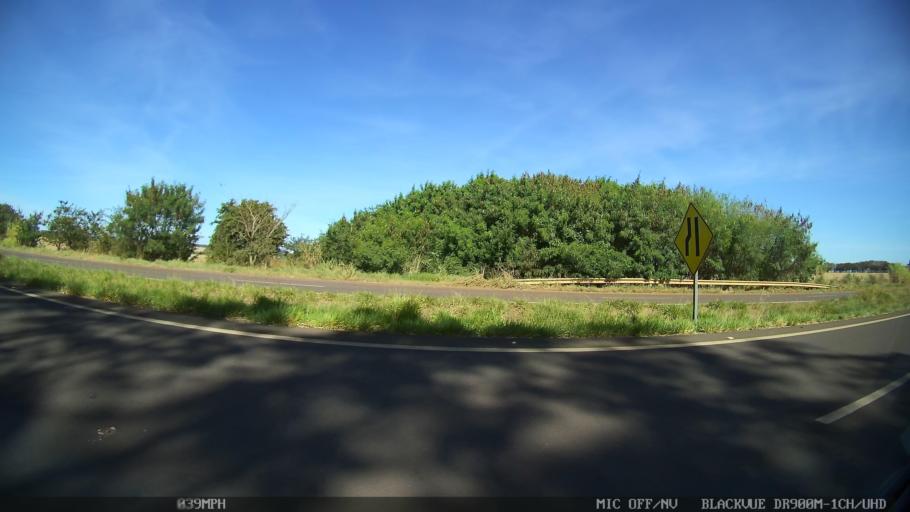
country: BR
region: Sao Paulo
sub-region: Franca
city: Franca
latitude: -20.5463
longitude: -47.4682
